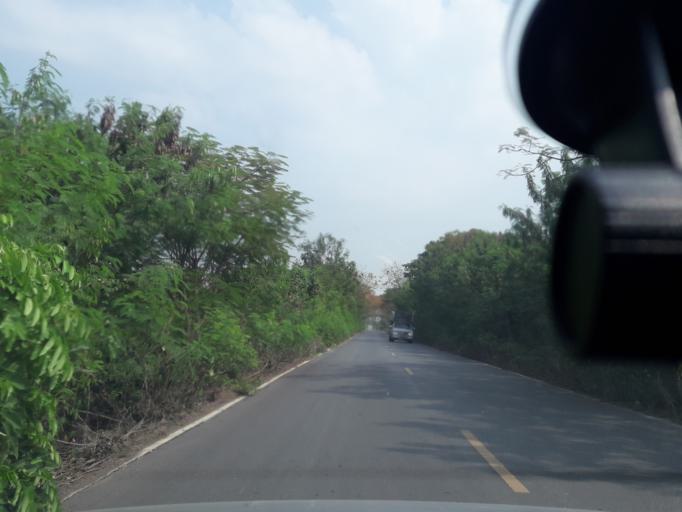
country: TH
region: Pathum Thani
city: Nong Suea
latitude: 14.1968
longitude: 100.8810
